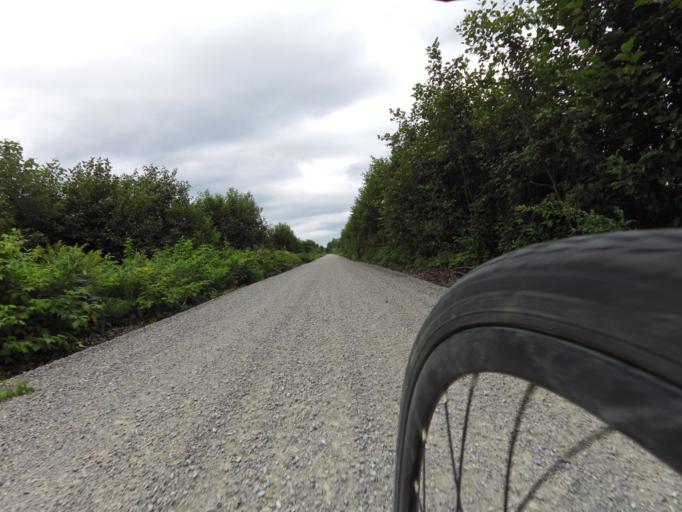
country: CA
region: Ontario
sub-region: Lanark County
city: Smiths Falls
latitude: 44.9487
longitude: -76.0432
